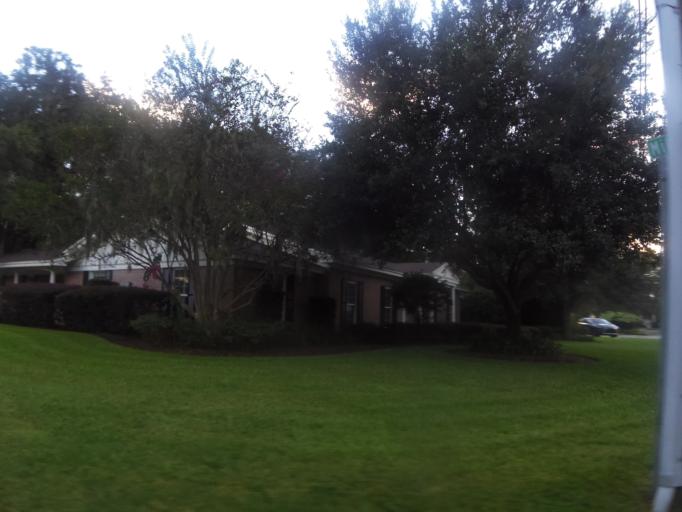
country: US
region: Florida
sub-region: Duval County
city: Jacksonville
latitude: 30.2359
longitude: -81.6236
